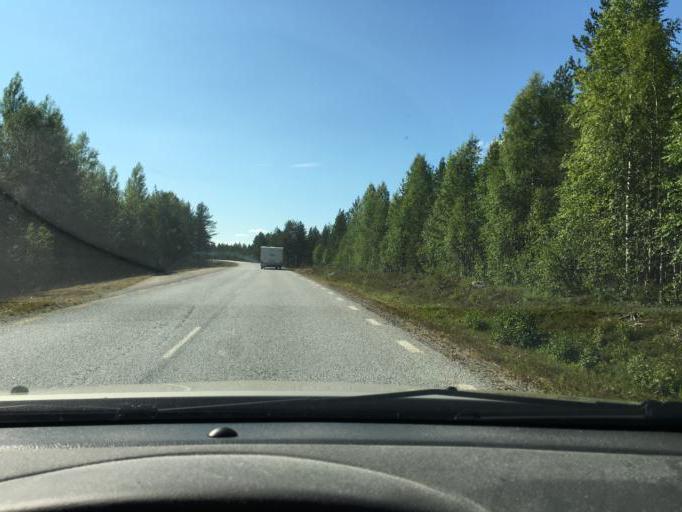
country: SE
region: Norrbotten
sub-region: Lulea Kommun
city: Ranea
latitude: 66.0487
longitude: 22.2566
